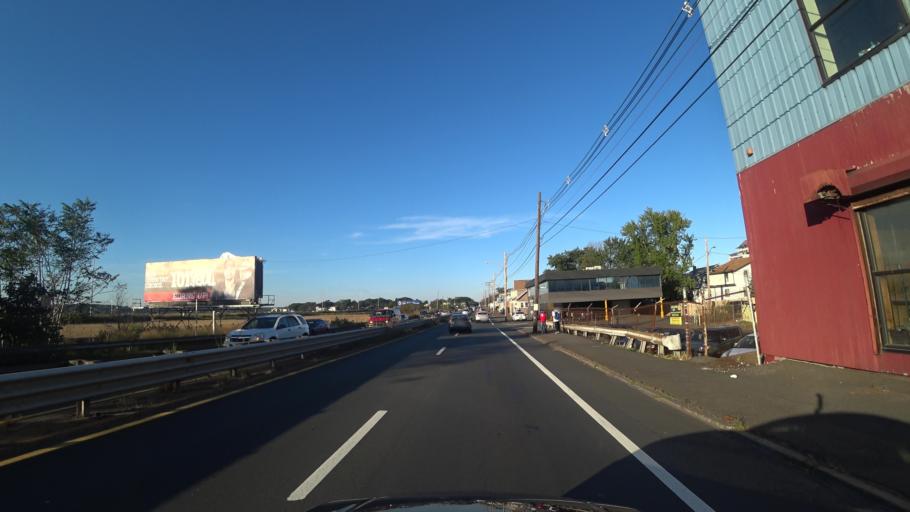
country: US
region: Massachusetts
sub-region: Suffolk County
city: Revere
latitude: 42.4197
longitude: -70.9903
